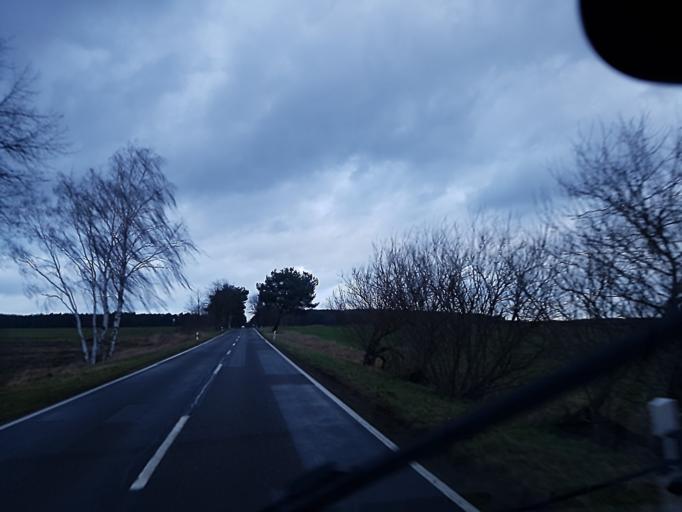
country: DE
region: Brandenburg
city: Plessa
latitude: 51.5395
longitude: 13.6661
